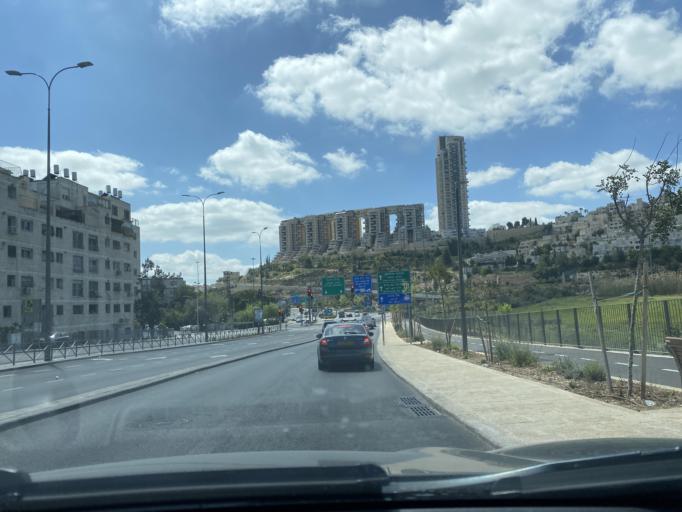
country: IL
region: Jerusalem
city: Jerusalem
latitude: 31.7570
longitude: 35.1957
